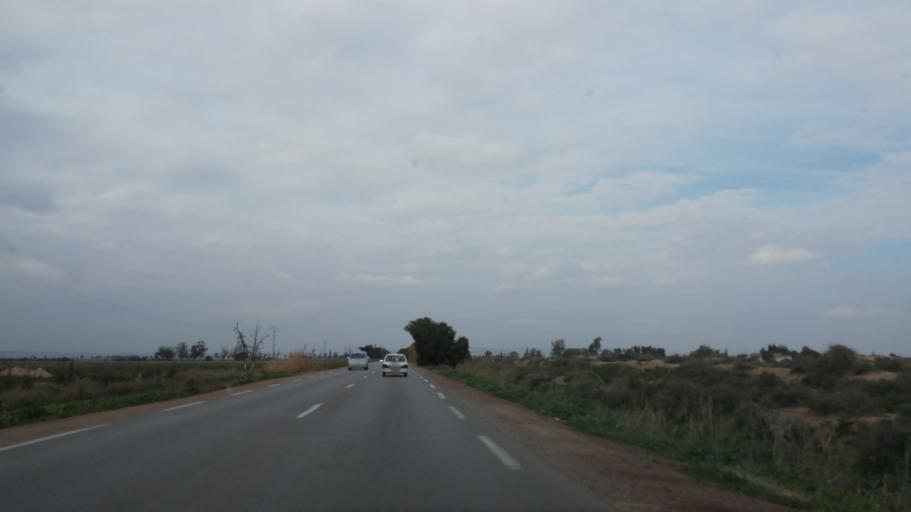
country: DZ
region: Mostaganem
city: Mostaganem
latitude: 35.6673
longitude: 0.0581
